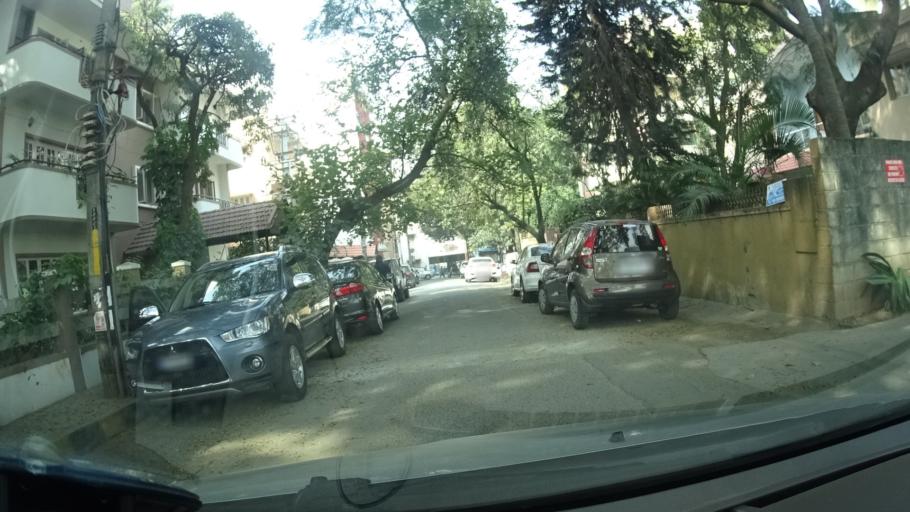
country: IN
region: Karnataka
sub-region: Bangalore Urban
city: Bangalore
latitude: 13.0025
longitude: 77.5660
